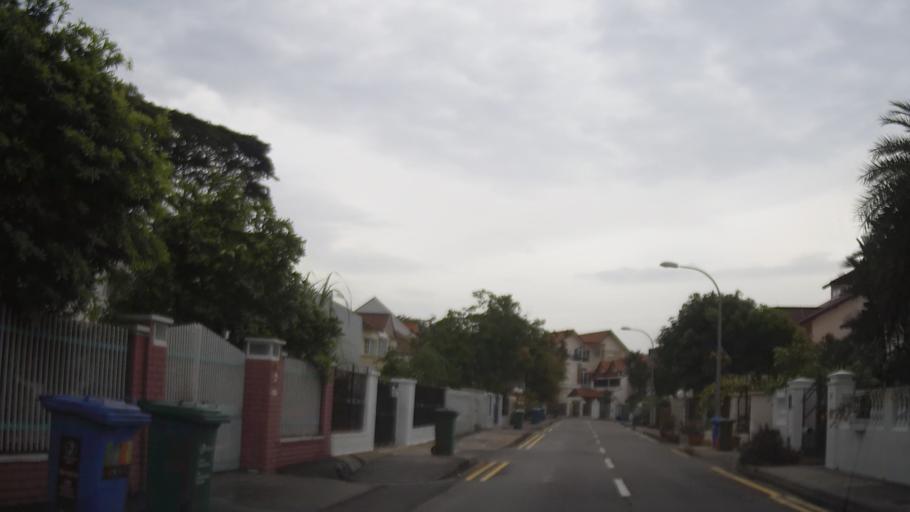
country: SG
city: Singapore
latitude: 1.3298
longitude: 103.8805
